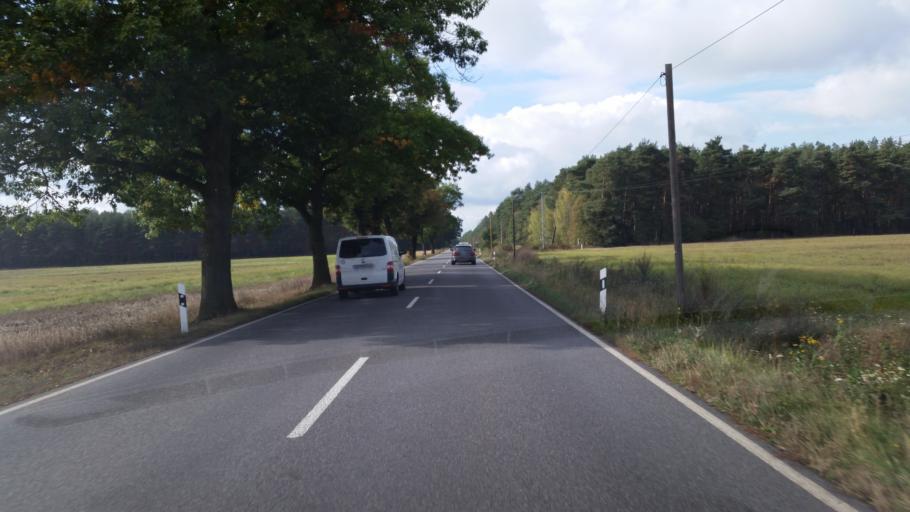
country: DE
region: Brandenburg
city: Grunewald
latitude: 51.4014
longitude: 13.9826
